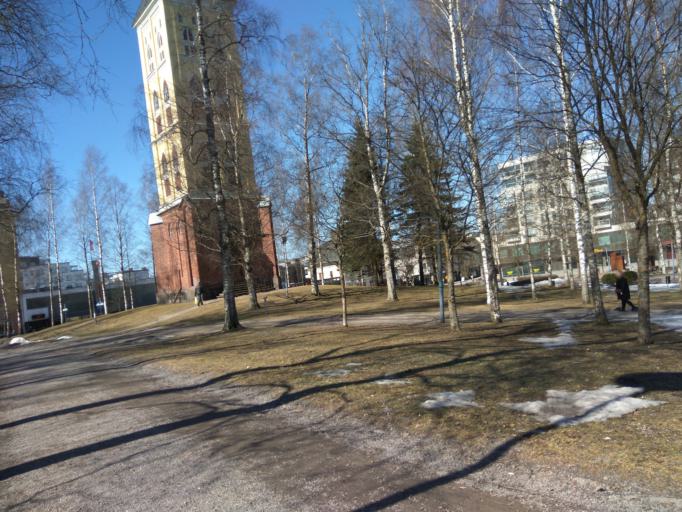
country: FI
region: South Karelia
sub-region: Lappeenranta
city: Lappeenranta
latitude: 61.0576
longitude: 28.1883
